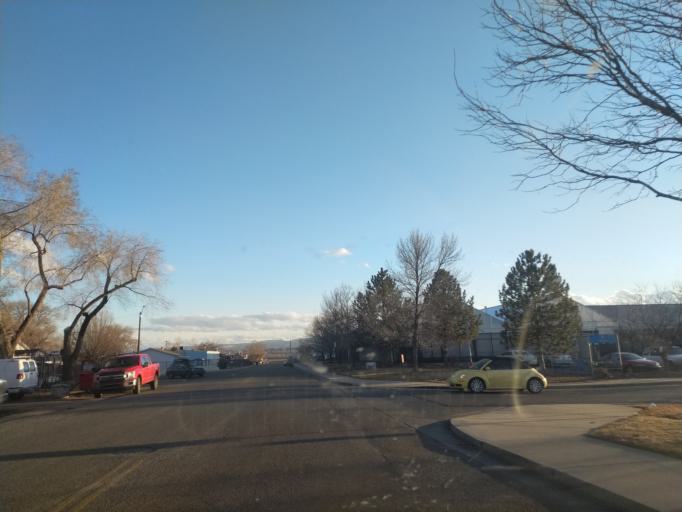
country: US
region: Colorado
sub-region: Mesa County
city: Fruitvale
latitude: 39.0762
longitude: -108.5175
